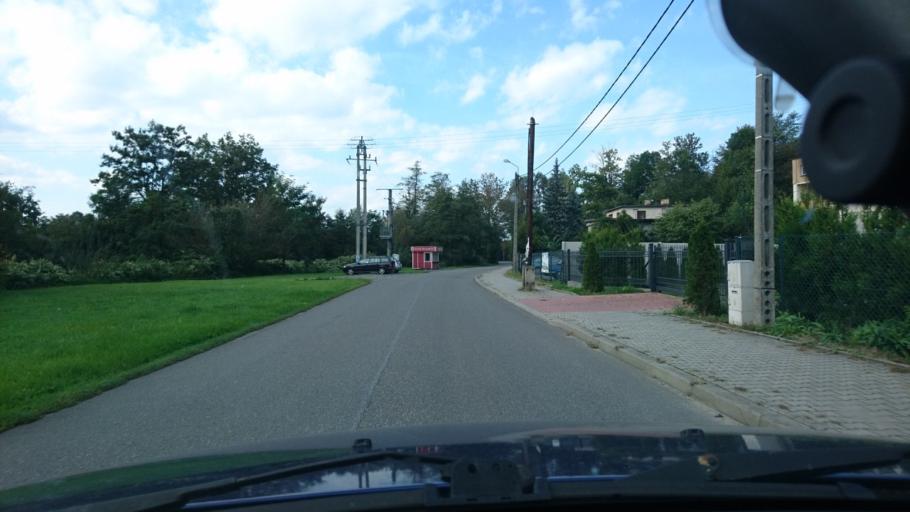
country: PL
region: Silesian Voivodeship
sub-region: Powiat bielski
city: Jasienica
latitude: 49.8153
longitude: 18.9221
